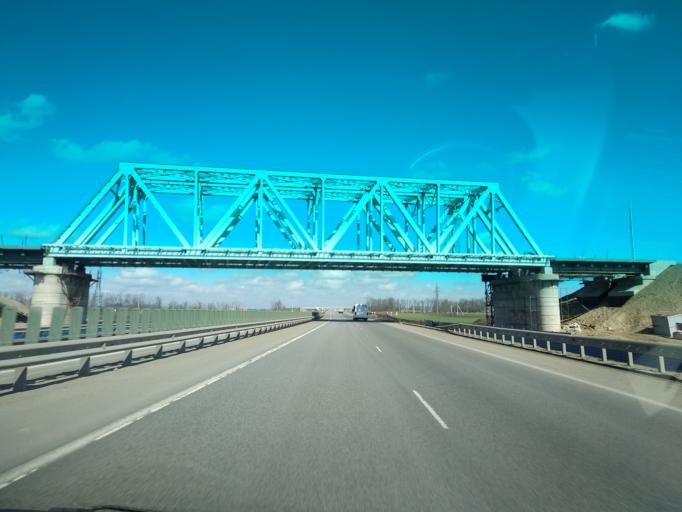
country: RU
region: Krasnodarskiy
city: Korenovsk
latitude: 45.4996
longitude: 39.4254
